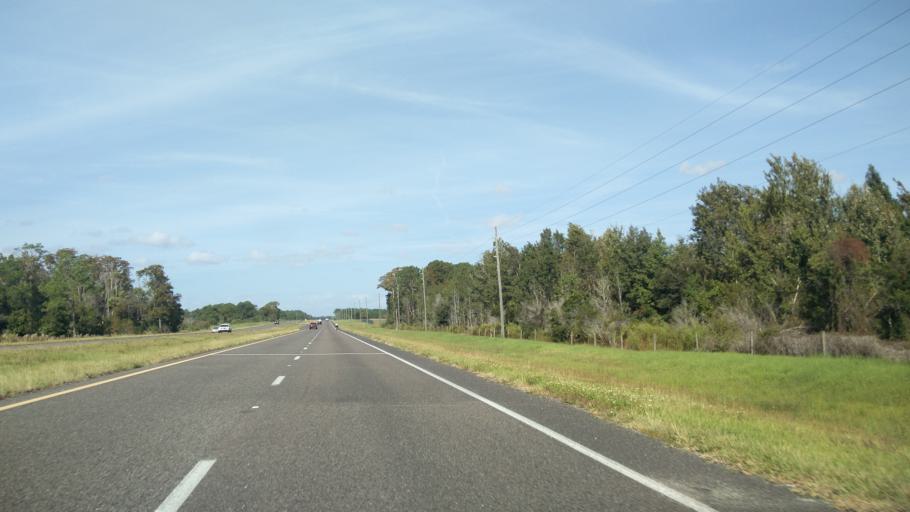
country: US
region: Florida
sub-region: Brevard County
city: June Park
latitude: 28.1031
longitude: -80.9017
